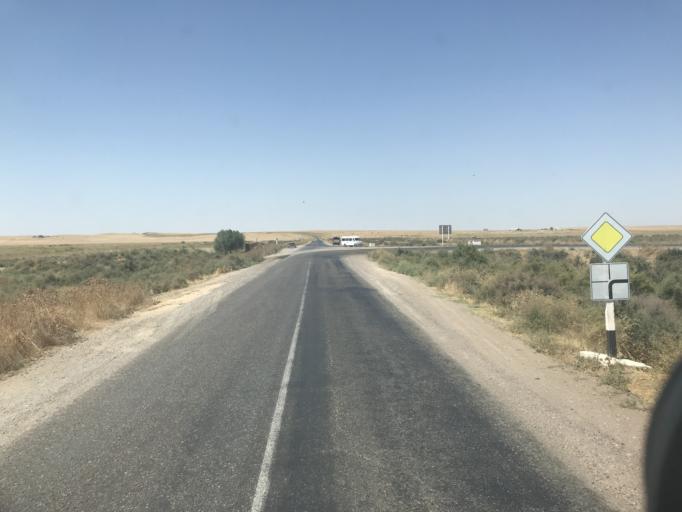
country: UZ
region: Toshkent
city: Chinoz
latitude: 41.2042
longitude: 68.5868
